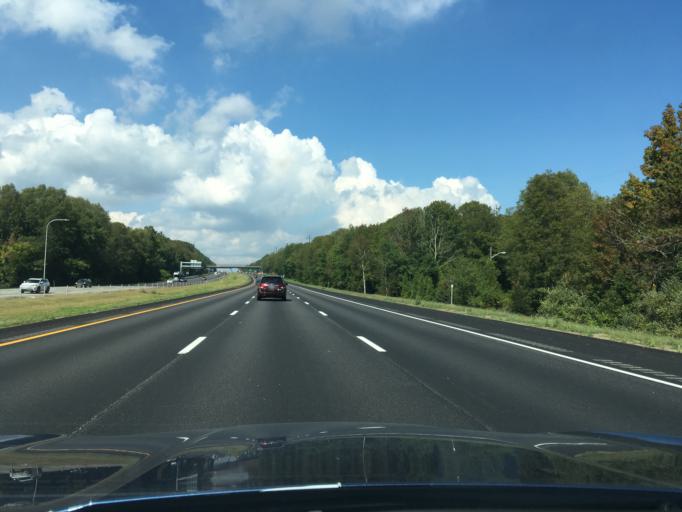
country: US
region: Rhode Island
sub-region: Kent County
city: East Greenwich
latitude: 41.6401
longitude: -71.4871
